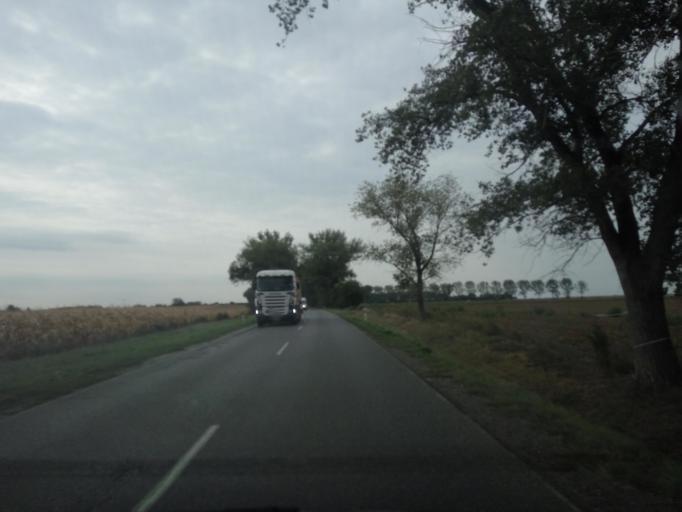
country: PL
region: Lower Silesian Voivodeship
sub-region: Powiat strzelinski
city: Strzelin
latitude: 50.8809
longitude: 17.0622
